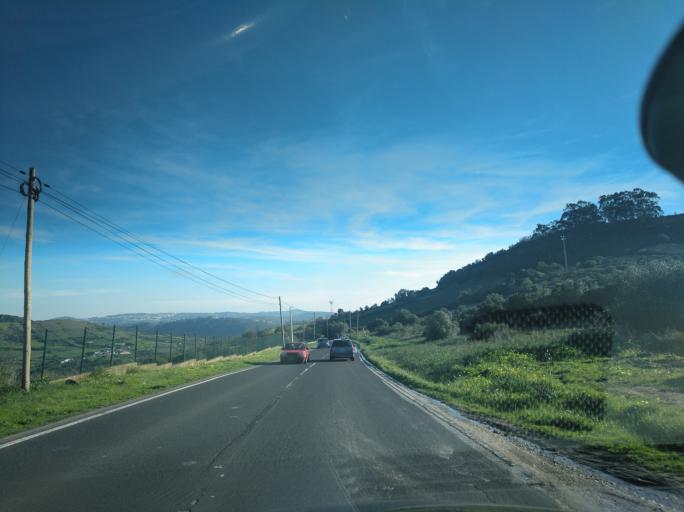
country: PT
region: Lisbon
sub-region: Mafra
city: Mafra
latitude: 38.9032
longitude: -9.3281
